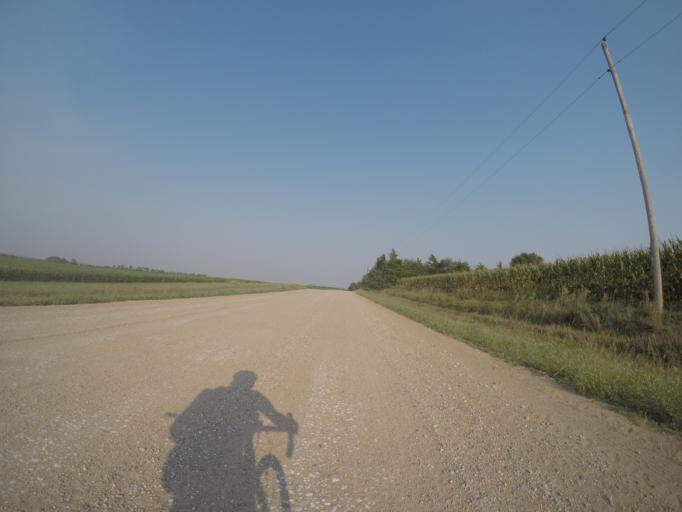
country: US
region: Nebraska
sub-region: Gage County
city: Beatrice
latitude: 40.2629
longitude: -96.8135
